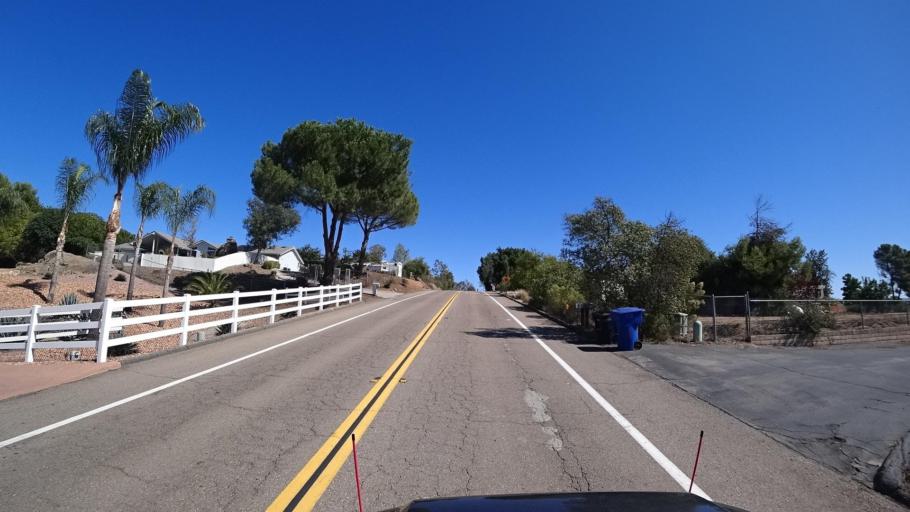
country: US
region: California
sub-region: San Diego County
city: Alpine
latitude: 32.8428
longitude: -116.7704
